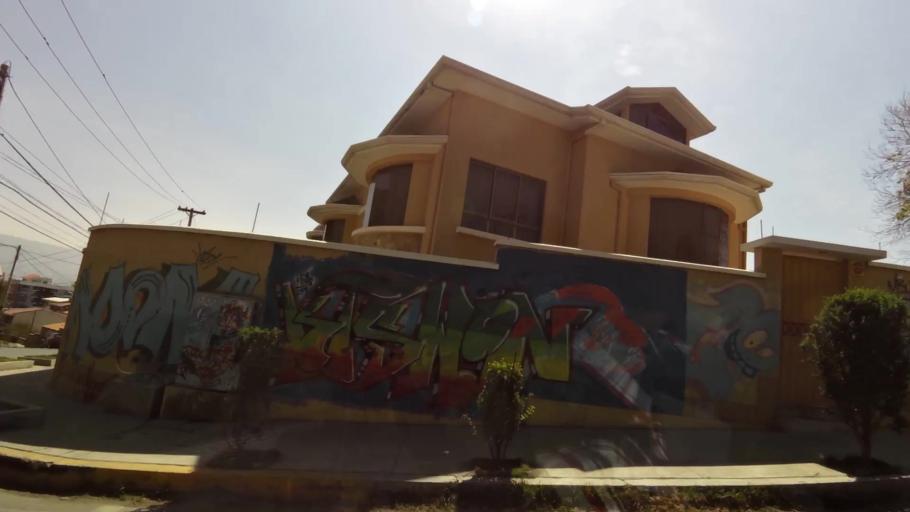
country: BO
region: La Paz
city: La Paz
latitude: -16.5415
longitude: -68.0582
